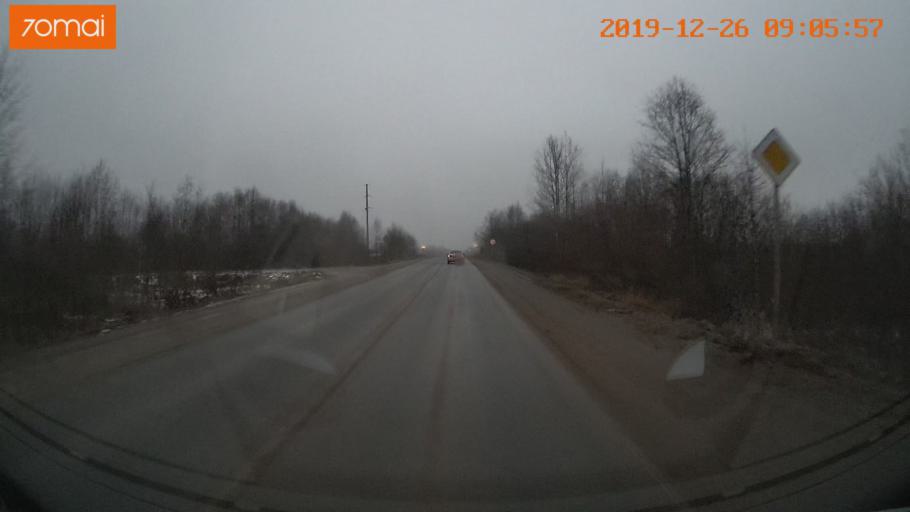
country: RU
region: Vologda
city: Gryazovets
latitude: 58.8310
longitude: 40.2555
